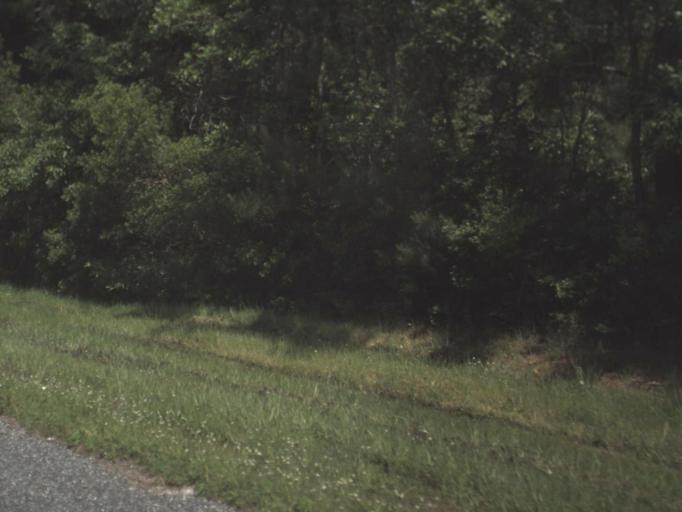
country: US
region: Florida
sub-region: Clay County
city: Middleburg
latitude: 29.9820
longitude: -81.9427
